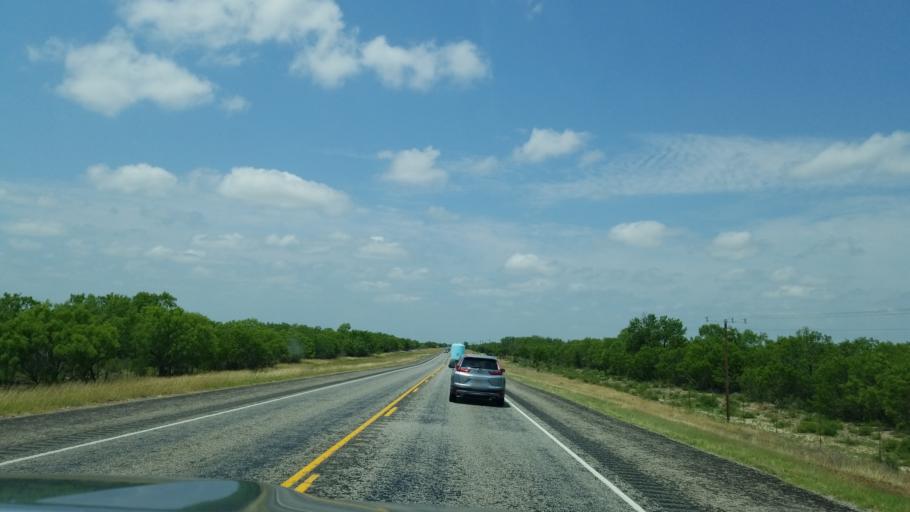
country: US
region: Texas
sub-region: Zavala County
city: La Pryor
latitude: 28.9321
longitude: -99.7520
